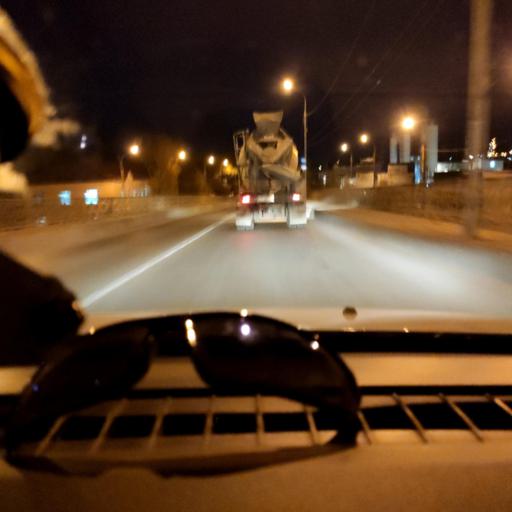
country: RU
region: Samara
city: Novokuybyshevsk
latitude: 53.1144
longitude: 50.0639
